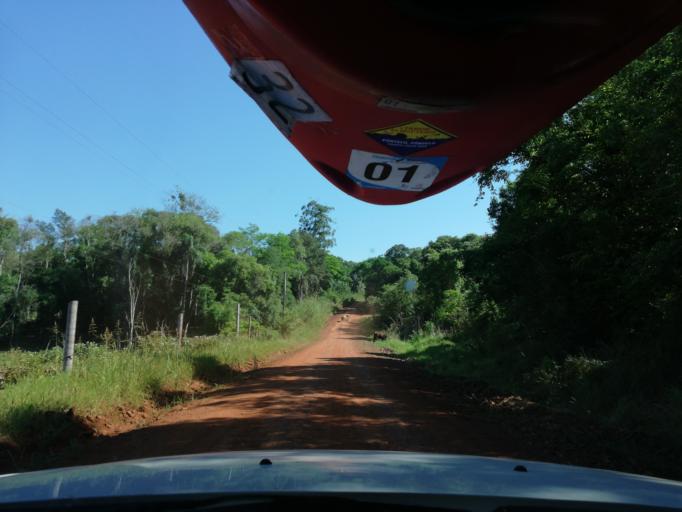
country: AR
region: Misiones
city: Puerto Leoni
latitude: -26.9703
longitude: -55.1646
